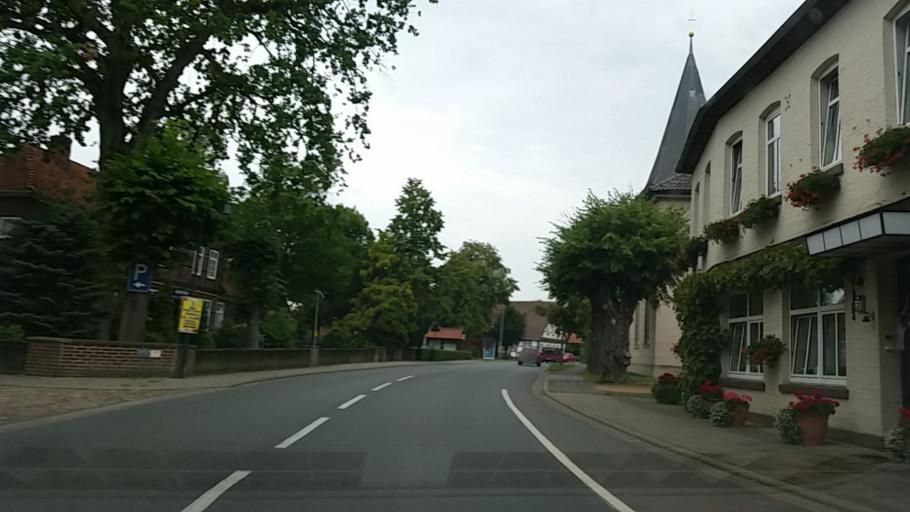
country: DE
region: Lower Saxony
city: Ahlden
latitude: 52.7594
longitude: 9.5565
